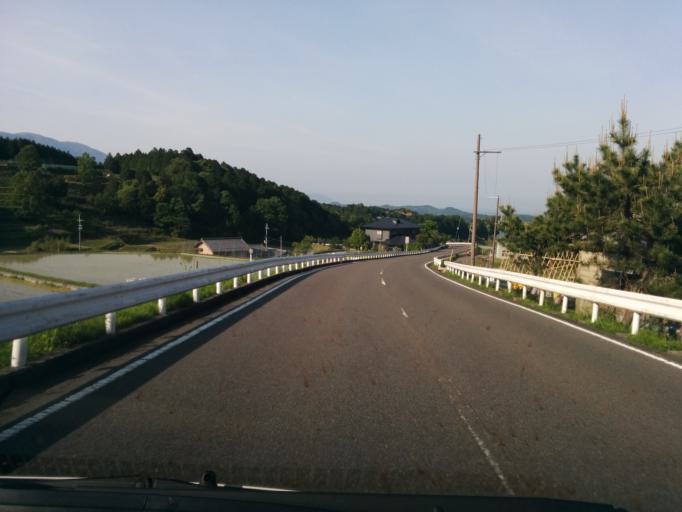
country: JP
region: Shiga Prefecture
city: Kitahama
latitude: 35.1039
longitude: 135.8669
